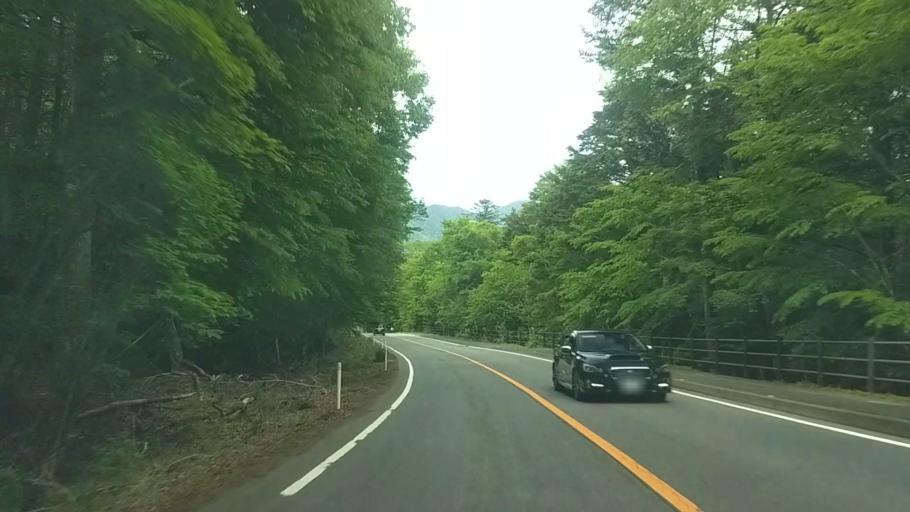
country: JP
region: Yamanashi
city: Fujikawaguchiko
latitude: 35.4909
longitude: 138.6488
